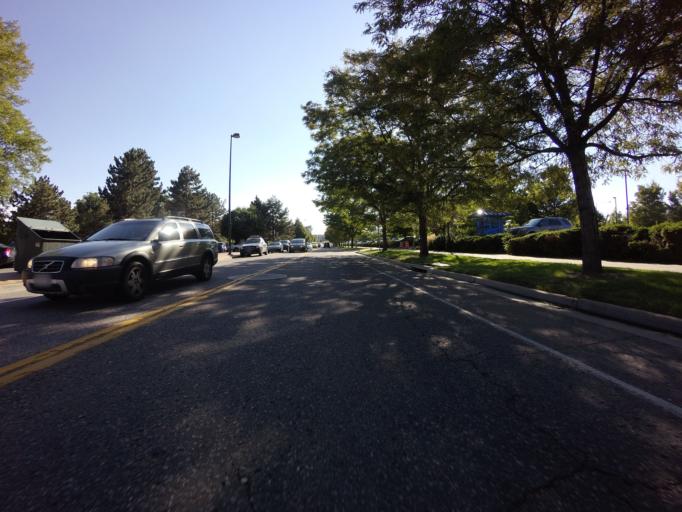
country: US
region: Colorado
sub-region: Denver County
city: Denver
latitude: 39.7536
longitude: -105.0113
